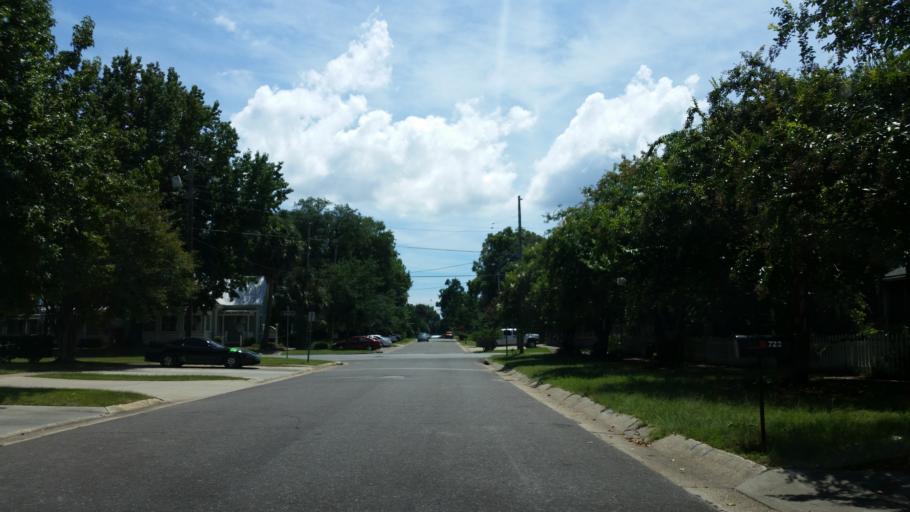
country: US
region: Florida
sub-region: Escambia County
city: Pensacola
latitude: 30.4224
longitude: -87.2082
